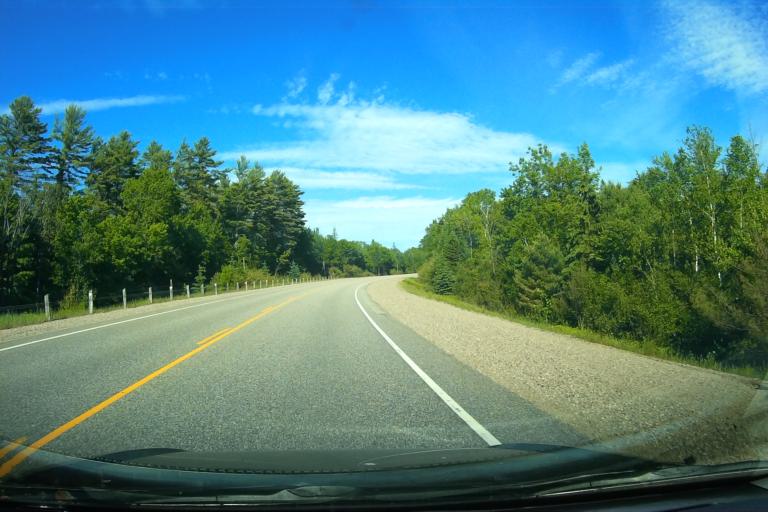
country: CA
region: Ontario
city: Deep River
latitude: 46.1799
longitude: -77.6754
